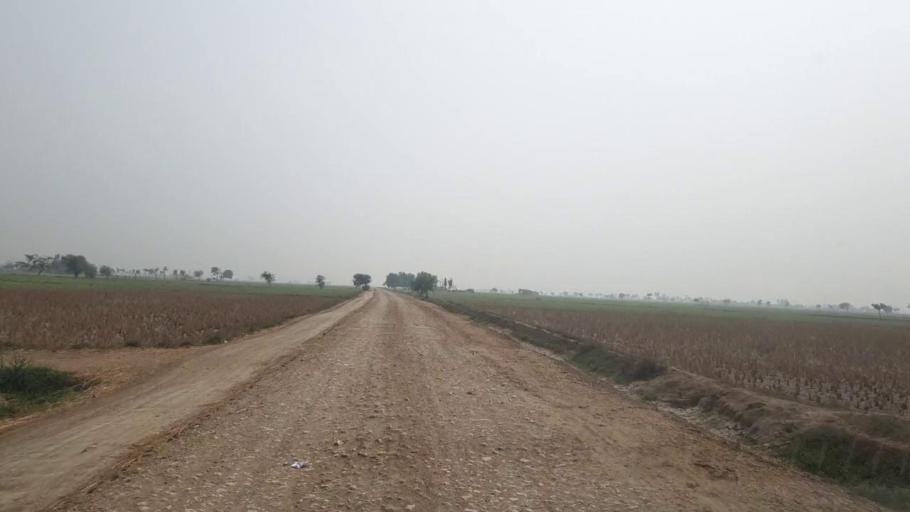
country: PK
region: Sindh
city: Kario
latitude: 24.6450
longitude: 68.5953
